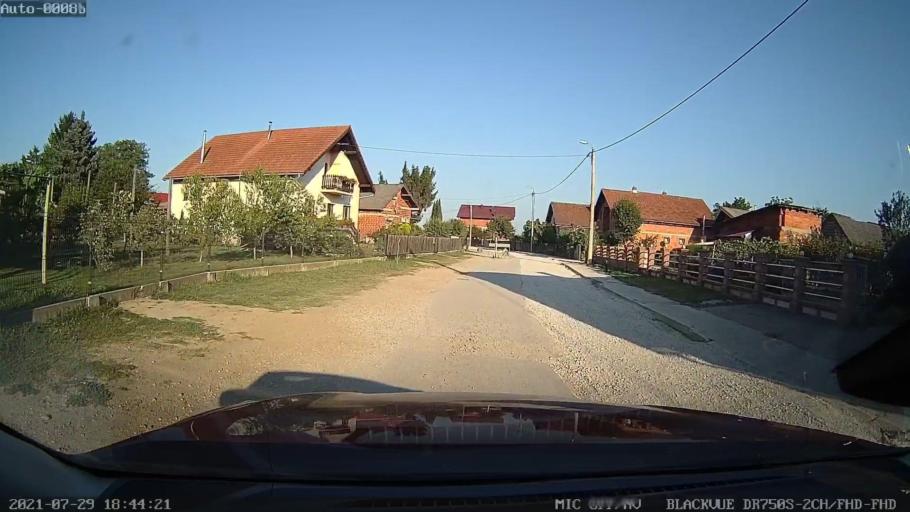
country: HR
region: Varazdinska
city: Petrijanec
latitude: 46.3167
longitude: 16.2377
